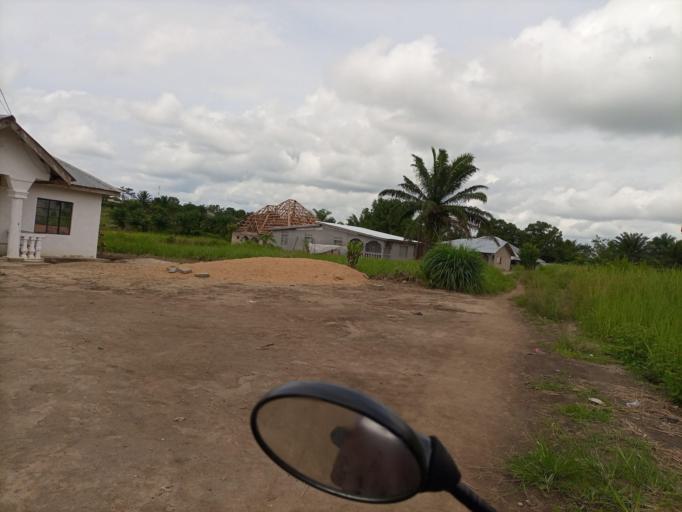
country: SL
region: Southern Province
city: Bo
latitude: 7.9698
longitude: -11.7680
